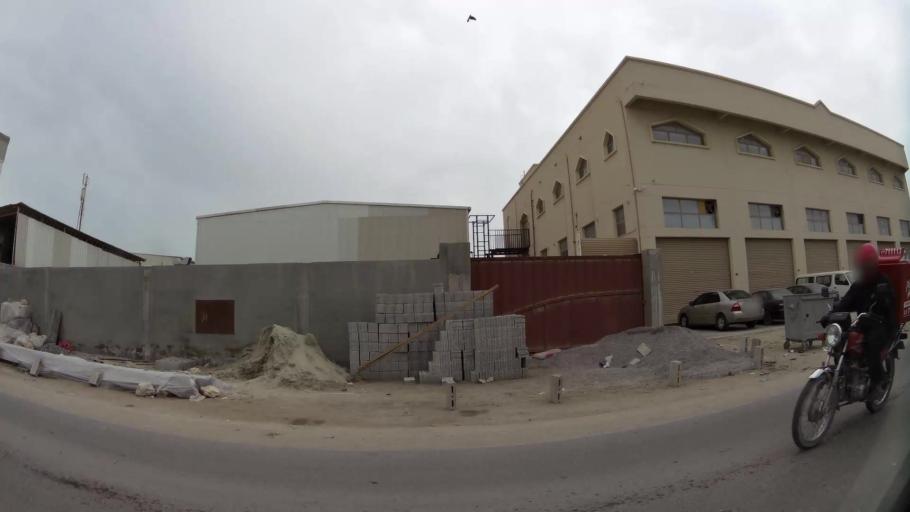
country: BH
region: Northern
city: Madinat `Isa
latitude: 26.1778
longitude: 50.5346
